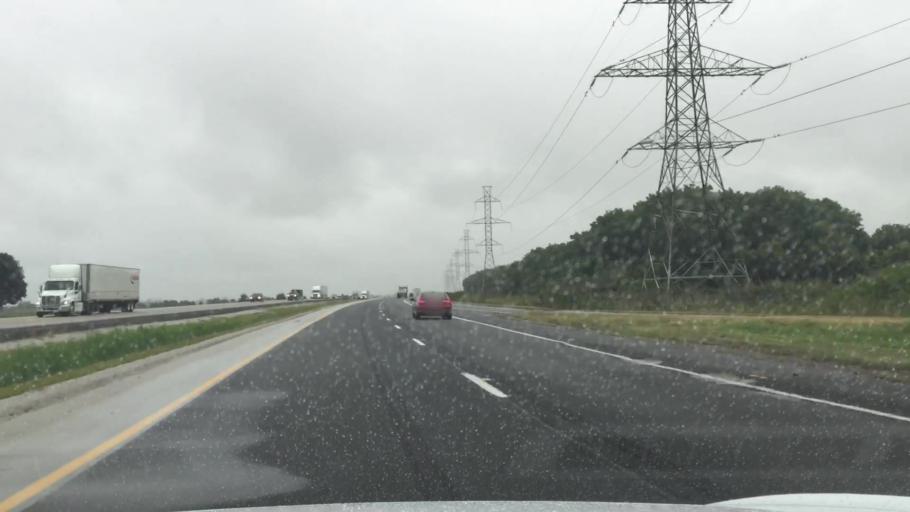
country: CA
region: Ontario
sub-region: Lambton County
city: Walpole Island
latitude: 42.3524
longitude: -82.1826
